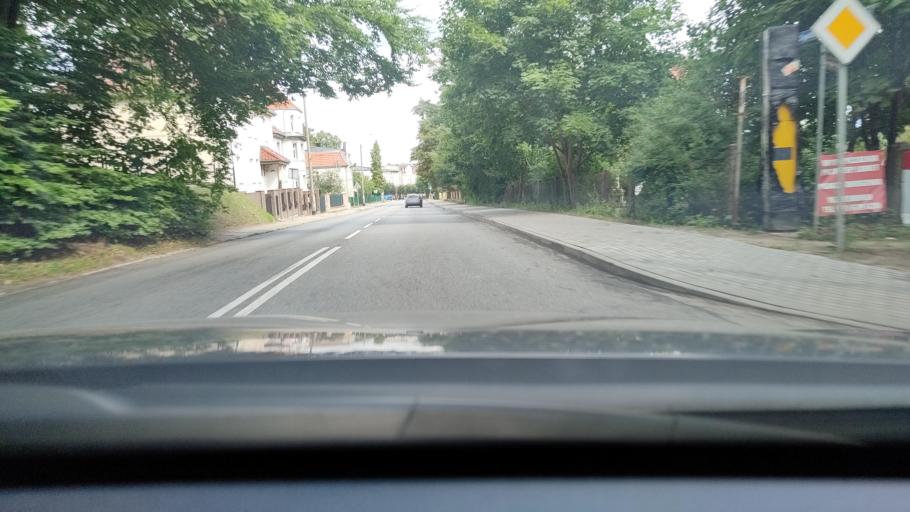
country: PL
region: Pomeranian Voivodeship
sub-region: Powiat wejherowski
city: Wejherowo
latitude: 54.5961
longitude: 18.2326
